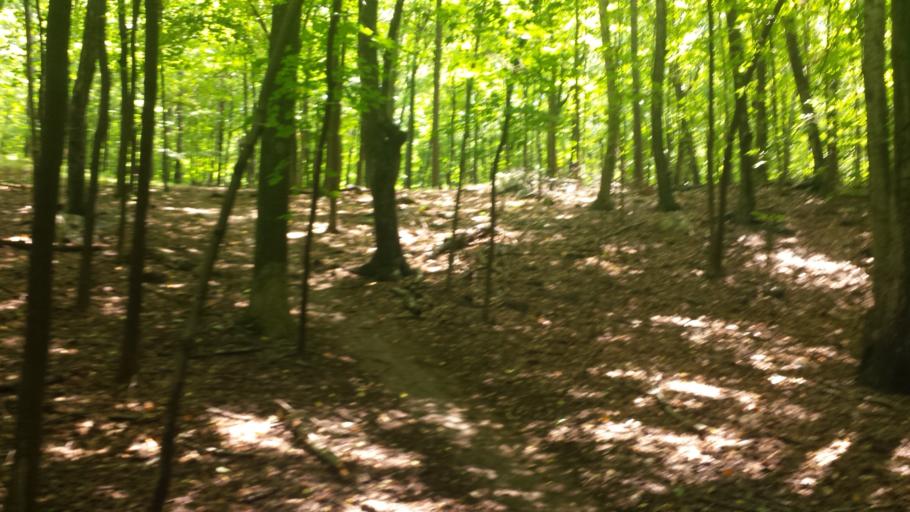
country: US
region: New York
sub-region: Westchester County
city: Hawthorne
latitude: 41.1210
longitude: -73.8027
